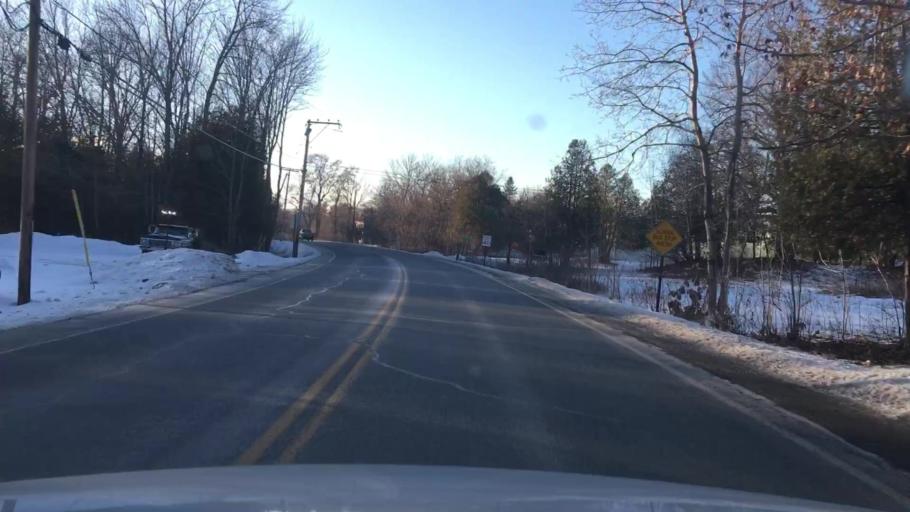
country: US
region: Maine
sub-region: Penobscot County
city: Eddington
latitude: 44.8301
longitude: -68.6643
